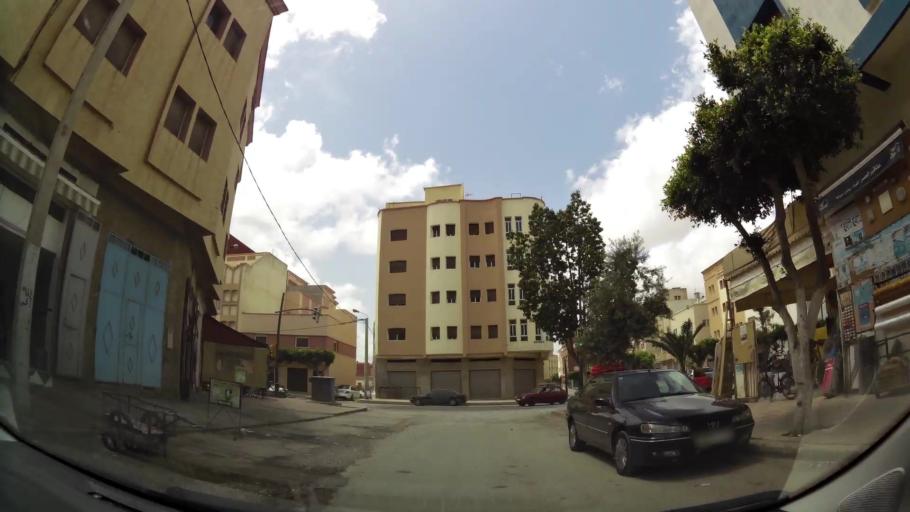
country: MA
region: Oriental
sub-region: Nador
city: Nador
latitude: 35.1689
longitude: -2.9191
